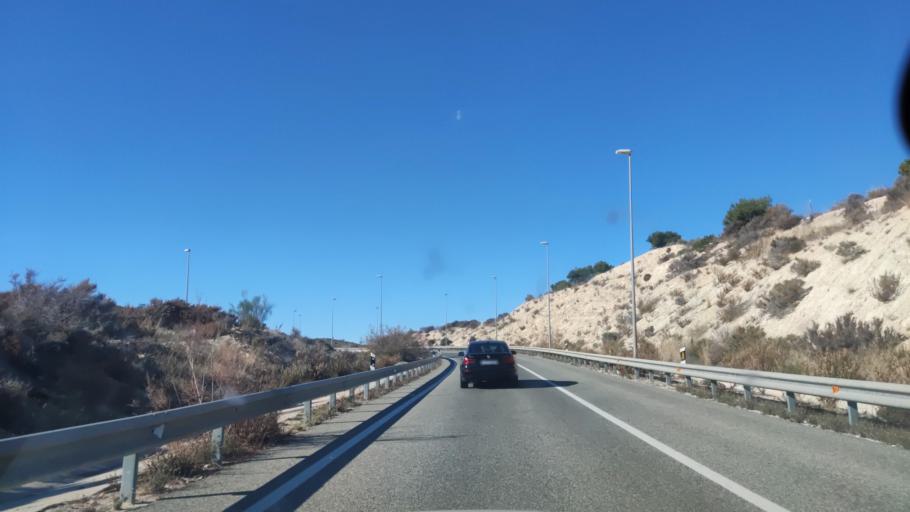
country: ES
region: Valencia
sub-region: Provincia de Alicante
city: el Campello
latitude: 38.4411
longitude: -0.4027
